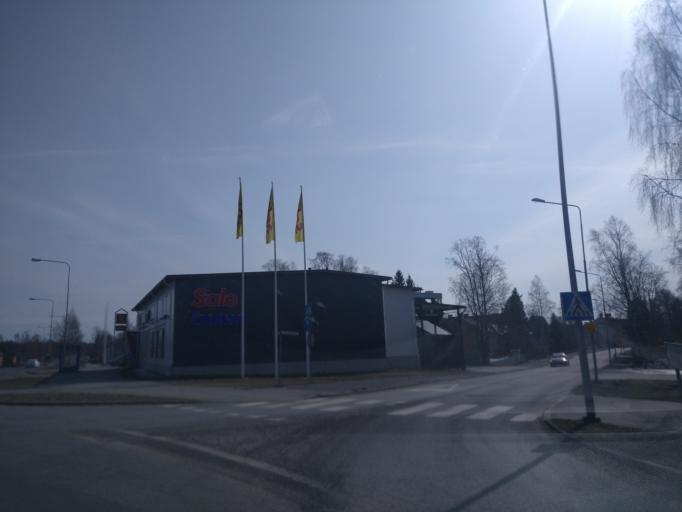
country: FI
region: Lapland
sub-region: Kemi-Tornio
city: Kemi
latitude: 65.7298
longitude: 24.5996
